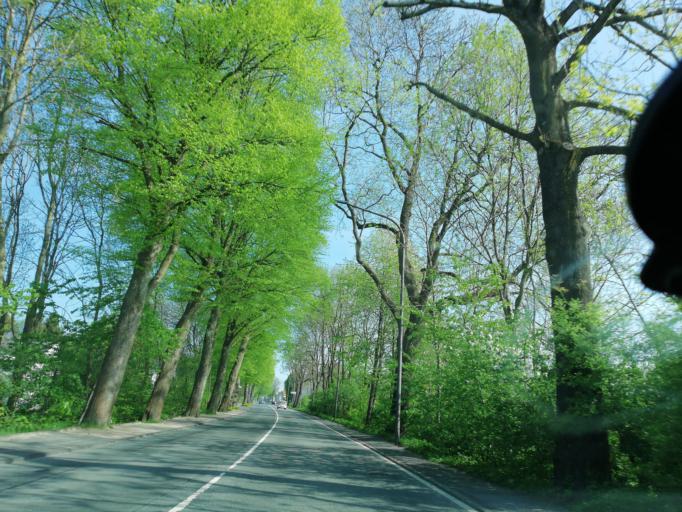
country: DE
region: North Rhine-Westphalia
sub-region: Regierungsbezirk Arnsberg
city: Schwelm
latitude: 51.3011
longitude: 7.2514
